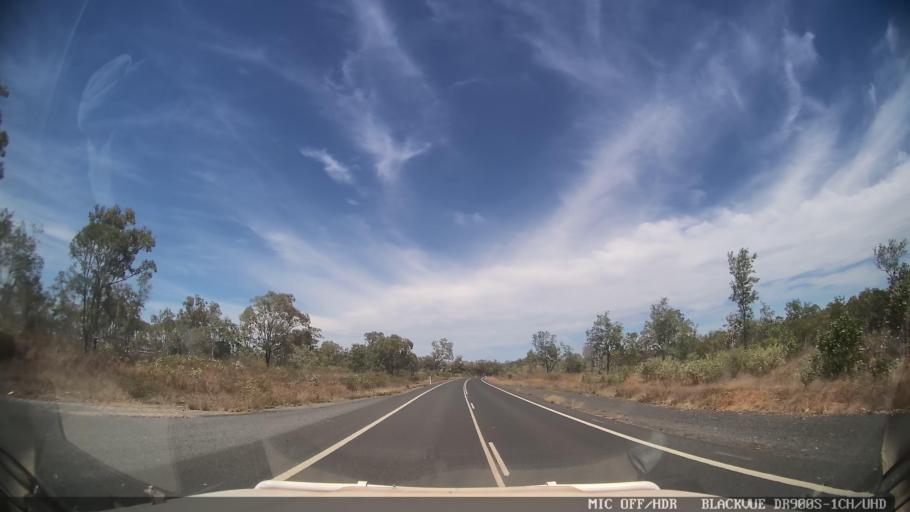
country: AU
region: Queensland
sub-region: Cook
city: Cooktown
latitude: -15.8714
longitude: 144.8604
